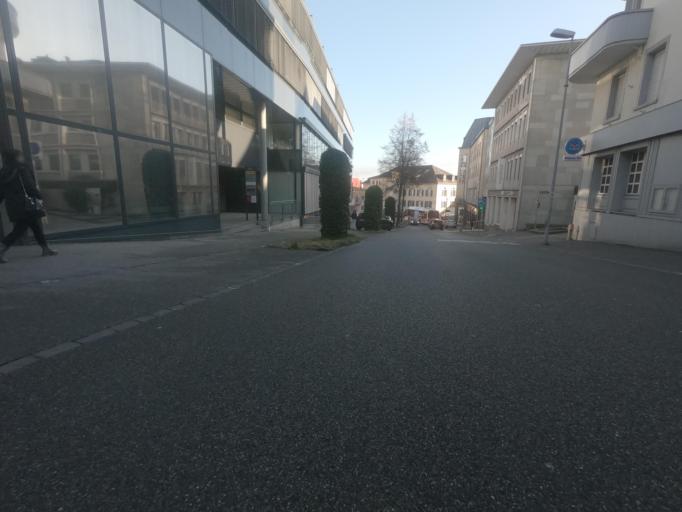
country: CH
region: Solothurn
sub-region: Bezirk Lebern
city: Grenchen
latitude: 47.1931
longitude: 7.3950
